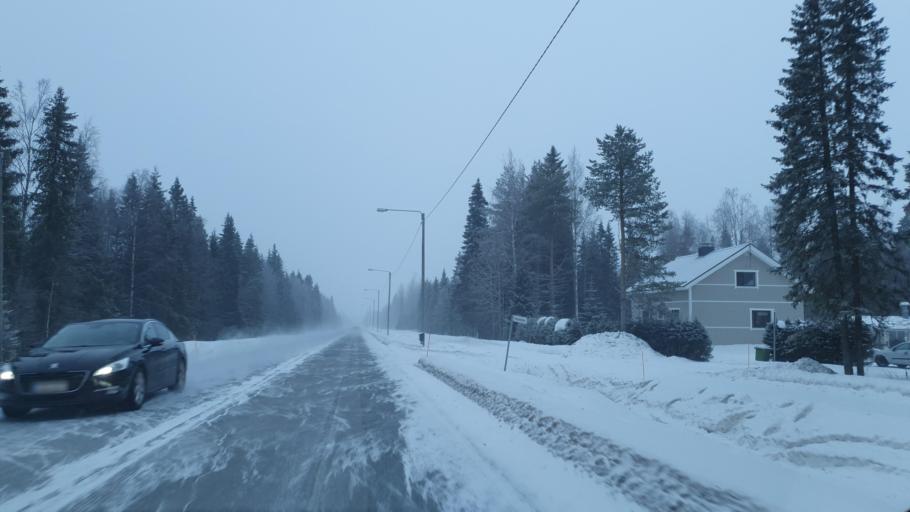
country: FI
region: Lapland
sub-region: Kemi-Tornio
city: Tornio
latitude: 66.0244
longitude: 24.0419
